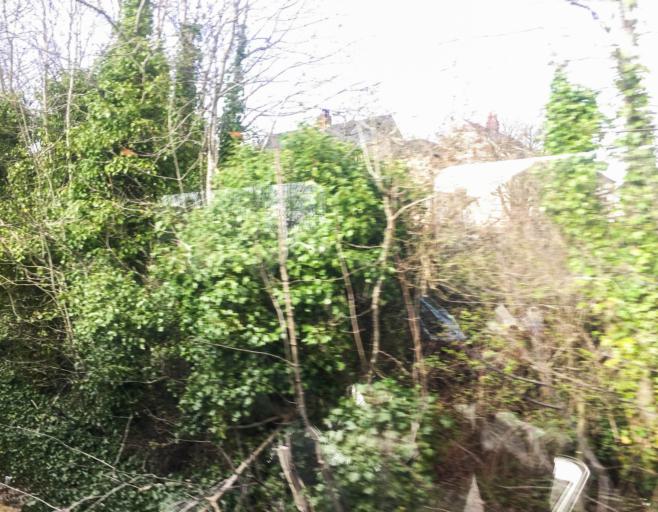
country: GB
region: Scotland
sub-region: North Lanarkshire
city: Wishaw
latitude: 55.7771
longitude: -3.9385
